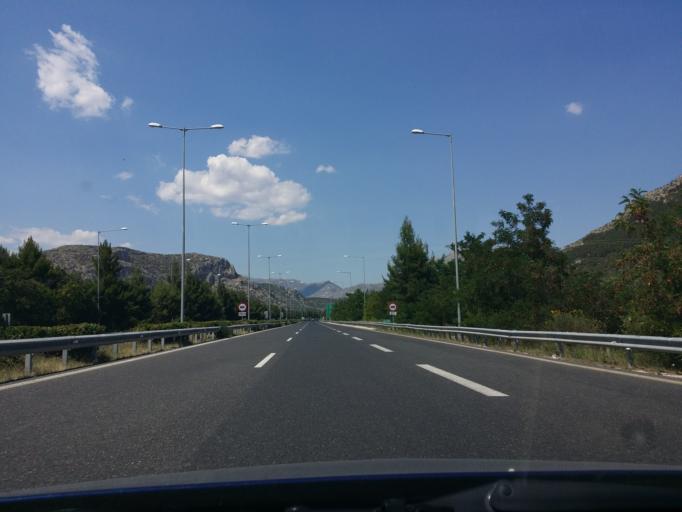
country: GR
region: Peloponnese
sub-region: Nomos Arkadias
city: Tripoli
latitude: 37.5827
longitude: 22.4327
